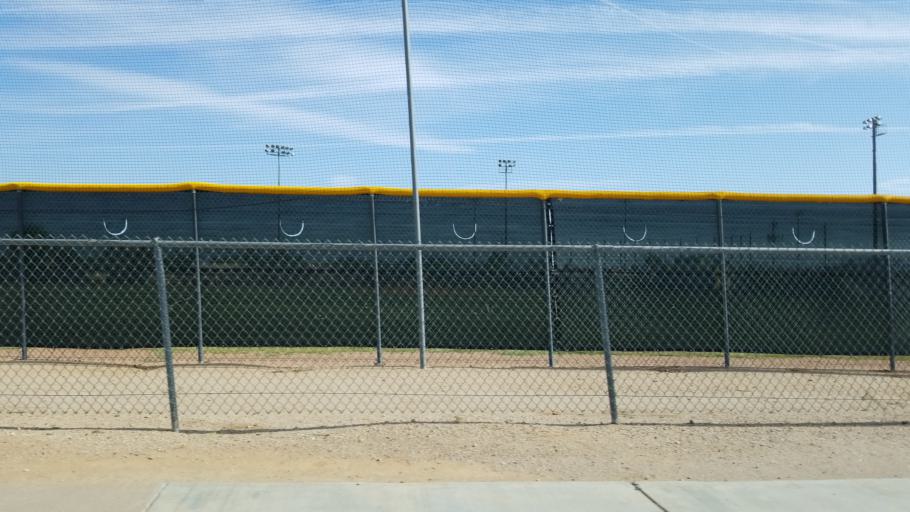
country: US
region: Arizona
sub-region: Maricopa County
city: Paradise Valley
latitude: 33.6258
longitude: -111.9546
